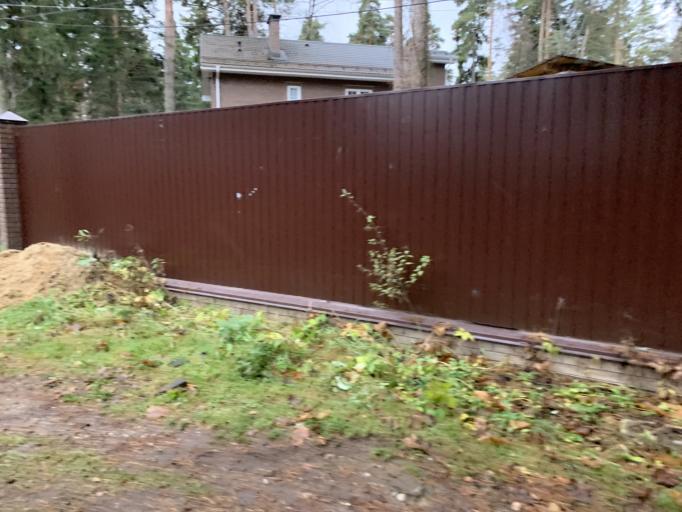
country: RU
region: Moskovskaya
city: Mamontovka
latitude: 55.9859
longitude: 37.8129
